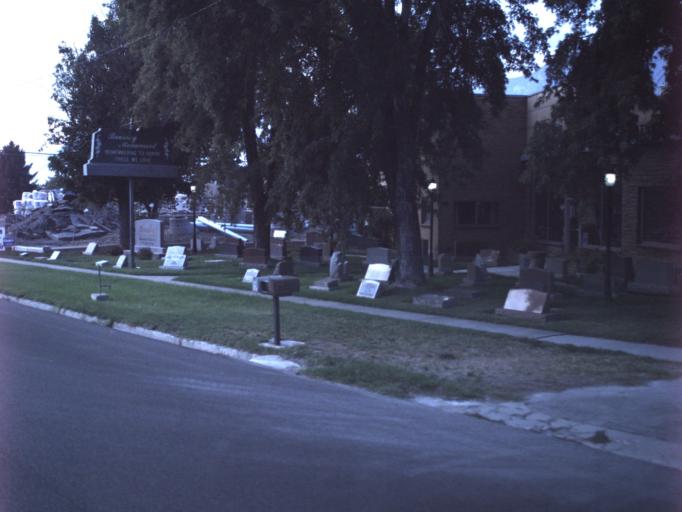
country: US
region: Utah
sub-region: Utah County
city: Provo
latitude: 40.2245
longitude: -111.6425
